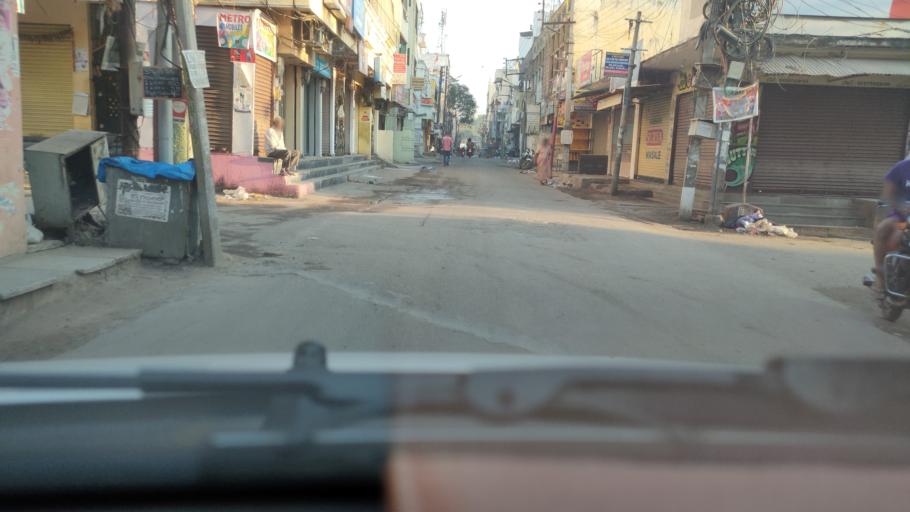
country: IN
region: Telangana
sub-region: Hyderabad
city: Malkajgiri
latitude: 17.4119
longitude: 78.5085
